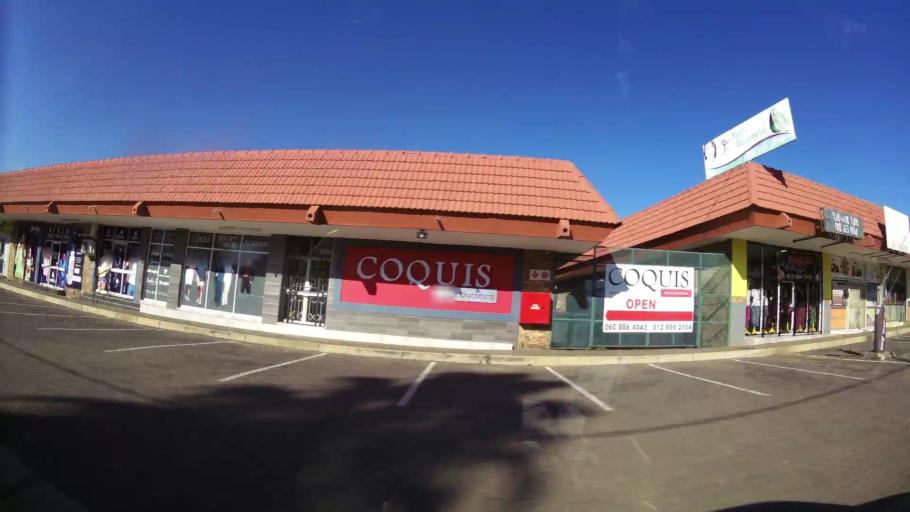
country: ZA
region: Gauteng
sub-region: City of Tshwane Metropolitan Municipality
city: Centurion
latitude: -25.8593
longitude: 28.1669
